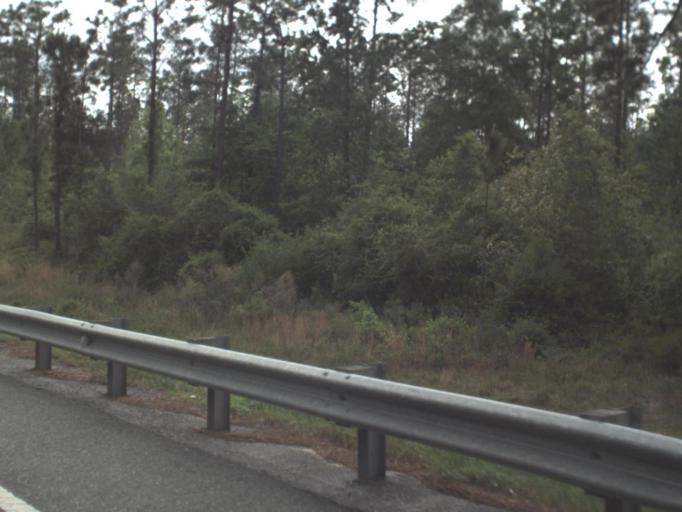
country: US
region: Alabama
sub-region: Escambia County
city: East Brewton
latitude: 30.8984
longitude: -87.0405
